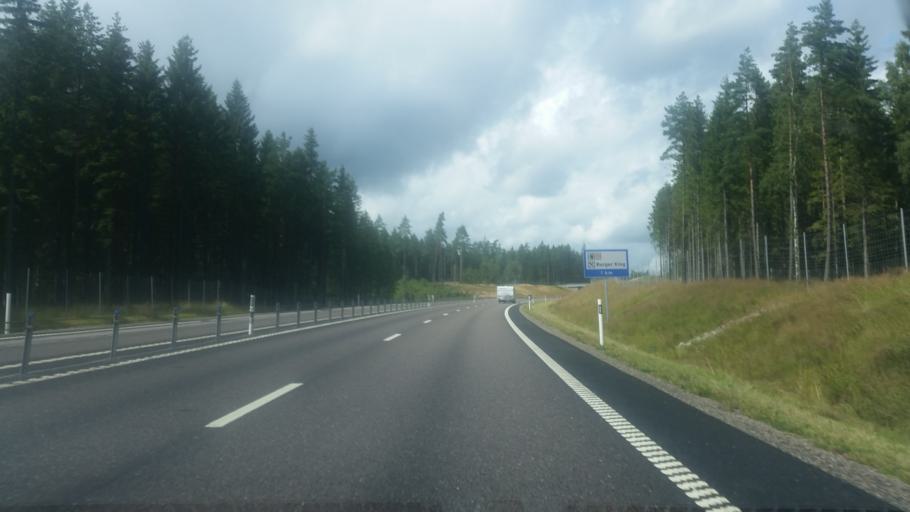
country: SE
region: Vaestra Goetaland
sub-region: Boras Kommun
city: Sjomarken
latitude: 57.7006
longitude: 12.8820
